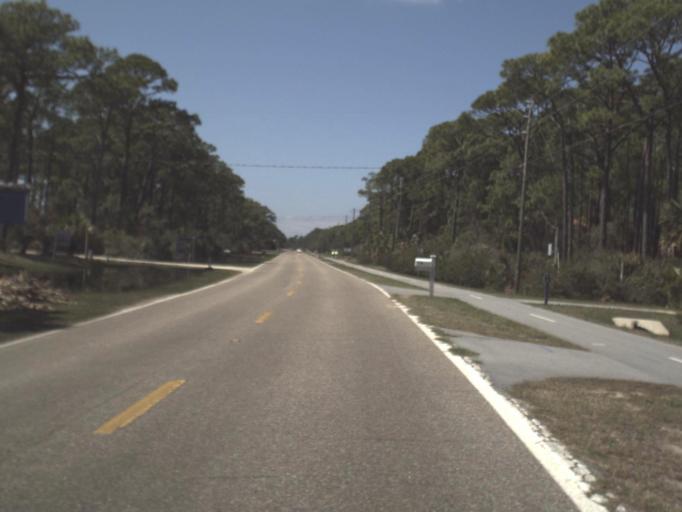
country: US
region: Florida
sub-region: Gulf County
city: Port Saint Joe
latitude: 29.6838
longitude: -85.3249
